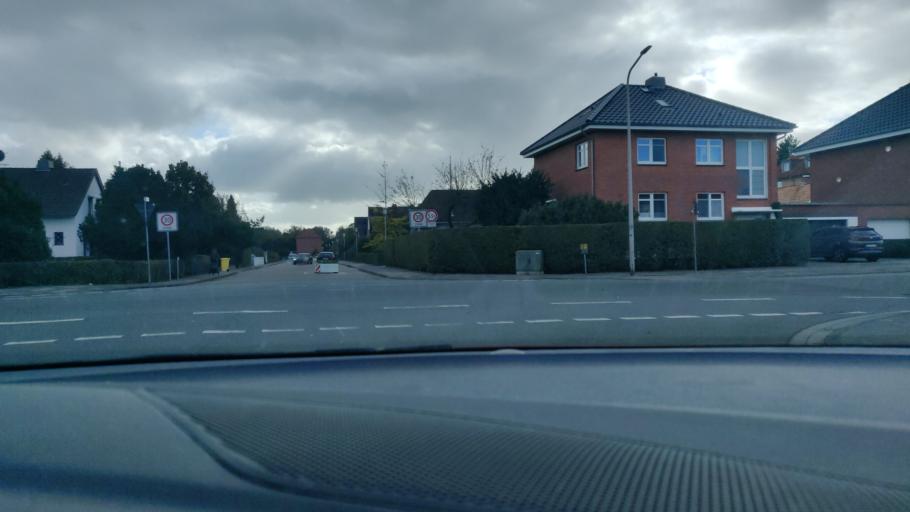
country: DE
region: Lower Saxony
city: Cuxhaven
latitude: 53.8689
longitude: 8.6900
